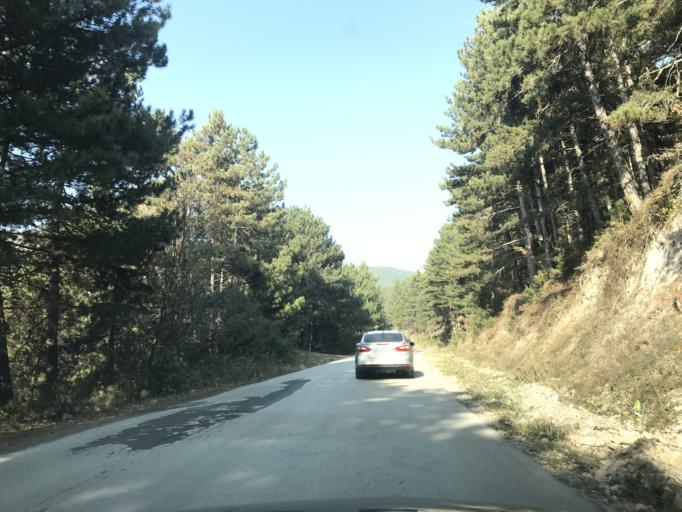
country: TR
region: Bolu
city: Bolu
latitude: 40.7825
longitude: 31.6328
